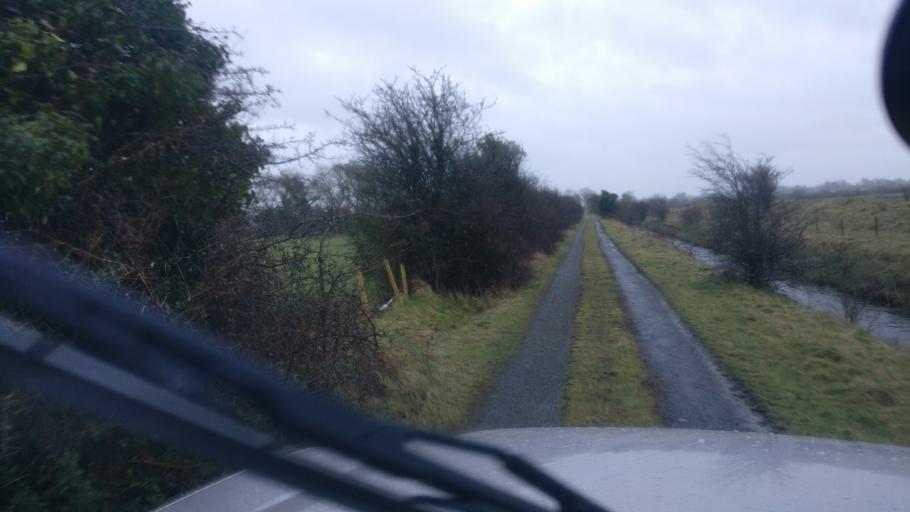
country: IE
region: Connaught
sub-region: County Galway
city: Ballinasloe
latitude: 53.2443
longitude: -8.3408
